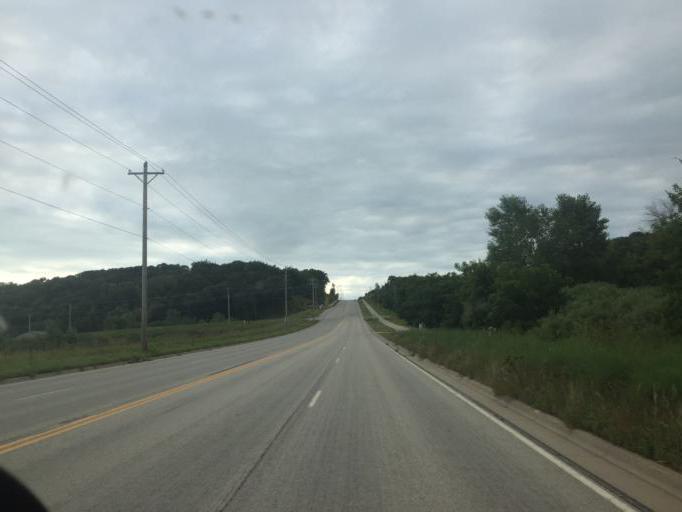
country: US
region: Minnesota
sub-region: Olmsted County
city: Rochester
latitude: 43.9640
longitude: -92.4765
